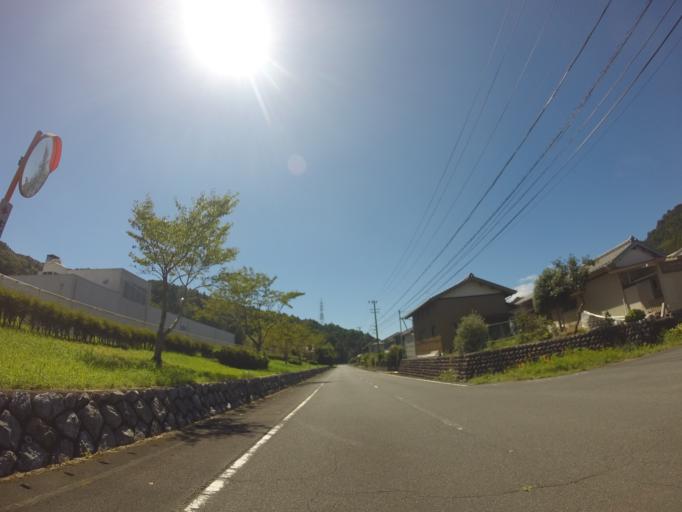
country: JP
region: Shizuoka
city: Kanaya
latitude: 34.8777
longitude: 138.1403
